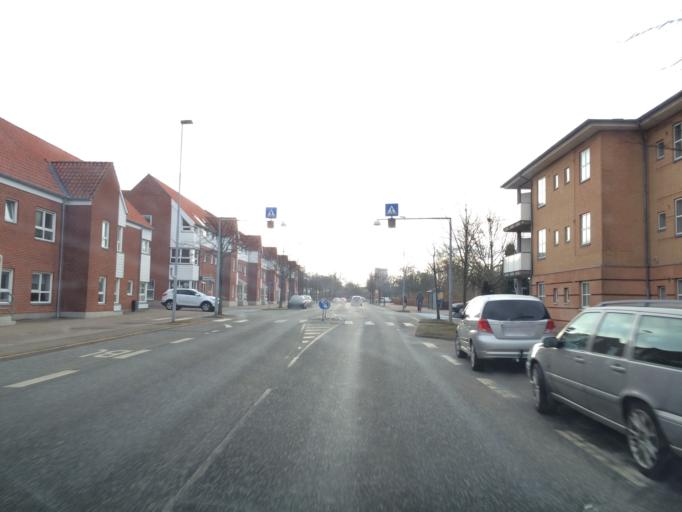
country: DK
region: South Denmark
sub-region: Fredericia Kommune
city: Fredericia
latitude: 55.5691
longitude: 9.7459
